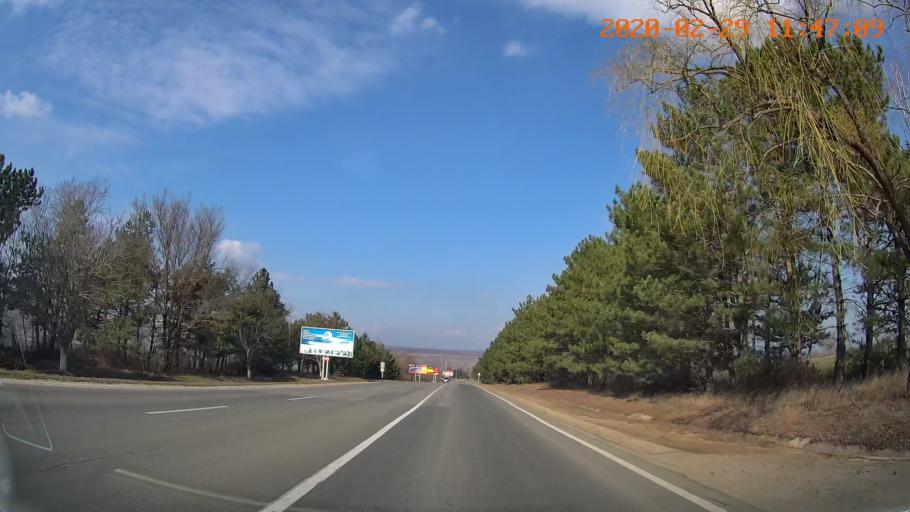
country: MD
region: Rezina
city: Rezina
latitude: 47.7382
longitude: 28.9898
